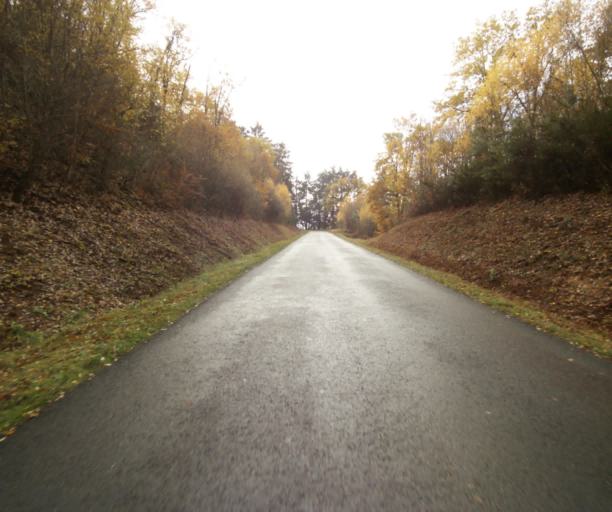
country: FR
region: Limousin
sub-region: Departement de la Correze
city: Cornil
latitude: 45.2282
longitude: 1.6485
